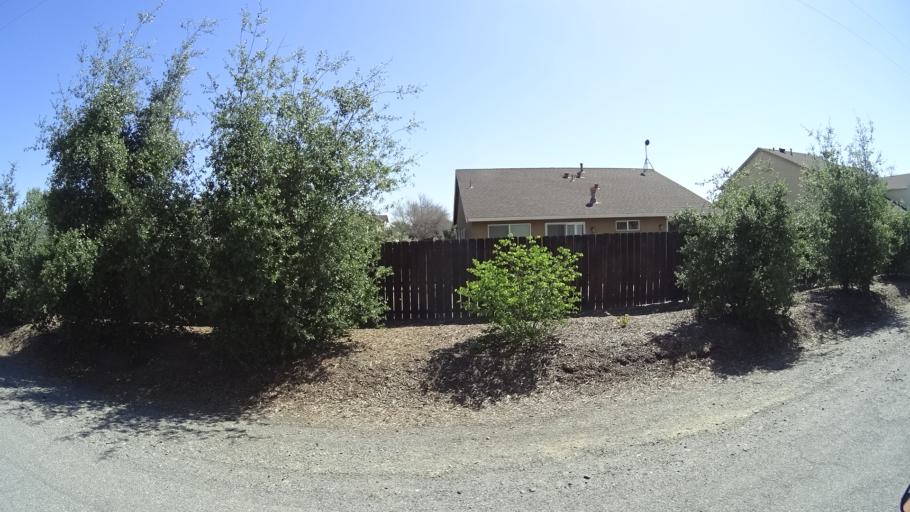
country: US
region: California
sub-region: Glenn County
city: Orland
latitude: 39.7591
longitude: -122.2015
